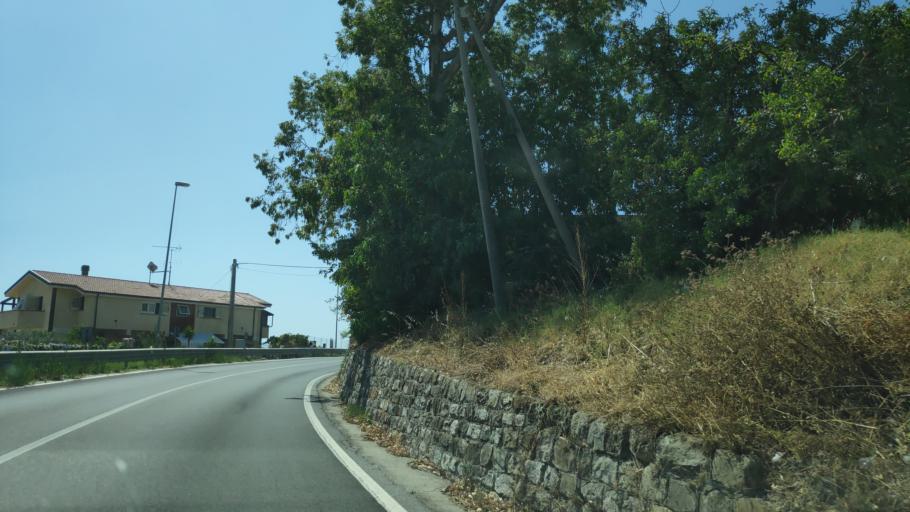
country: IT
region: Calabria
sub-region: Provincia di Reggio Calabria
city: Africo Nuovo
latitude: 38.0170
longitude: 16.1337
